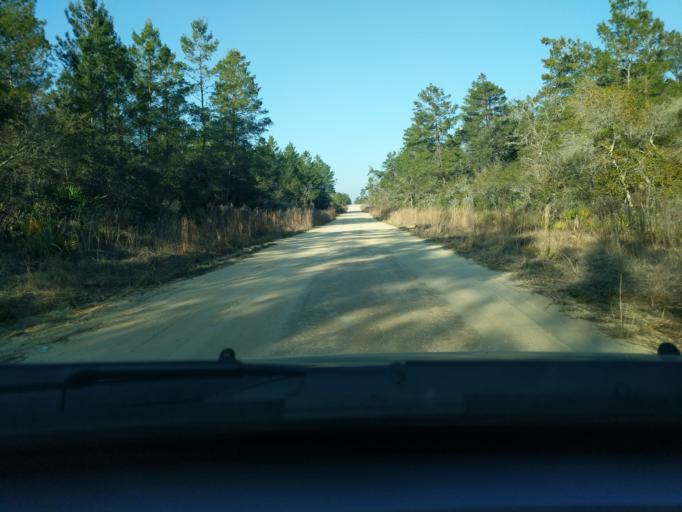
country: US
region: Florida
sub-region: Marion County
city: Silver Springs Shores
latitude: 29.2264
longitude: -81.8079
